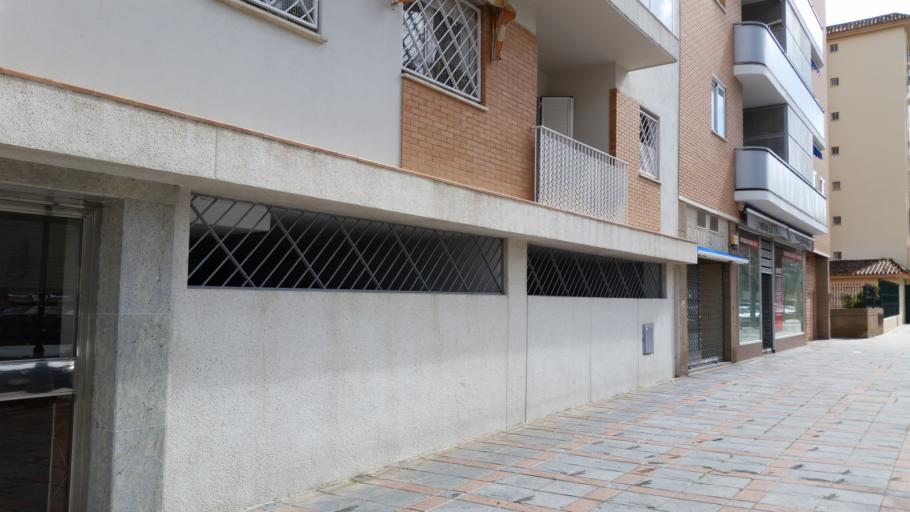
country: ES
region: Andalusia
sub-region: Provincia de Malaga
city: Fuengirola
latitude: 36.5477
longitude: -4.6195
